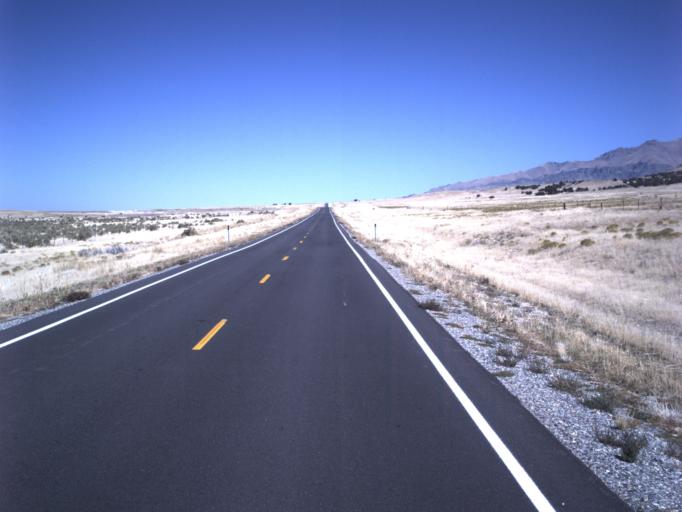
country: US
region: Utah
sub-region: Tooele County
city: Grantsville
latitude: 40.5609
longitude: -112.7353
